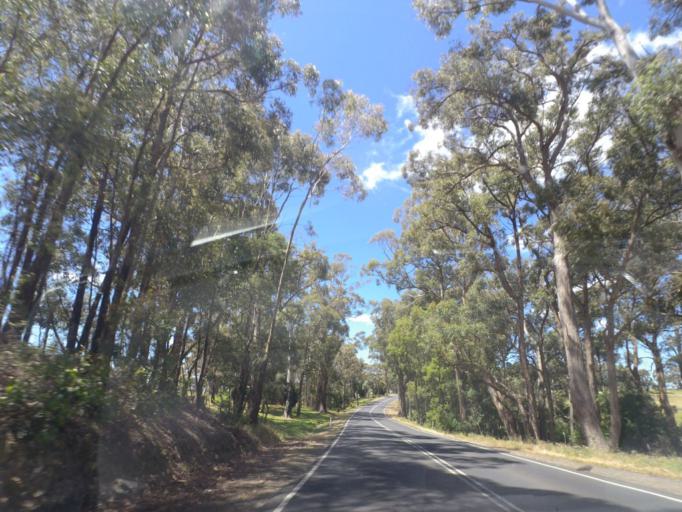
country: AU
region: Victoria
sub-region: Mount Alexander
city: Castlemaine
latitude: -37.2899
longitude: 144.2677
